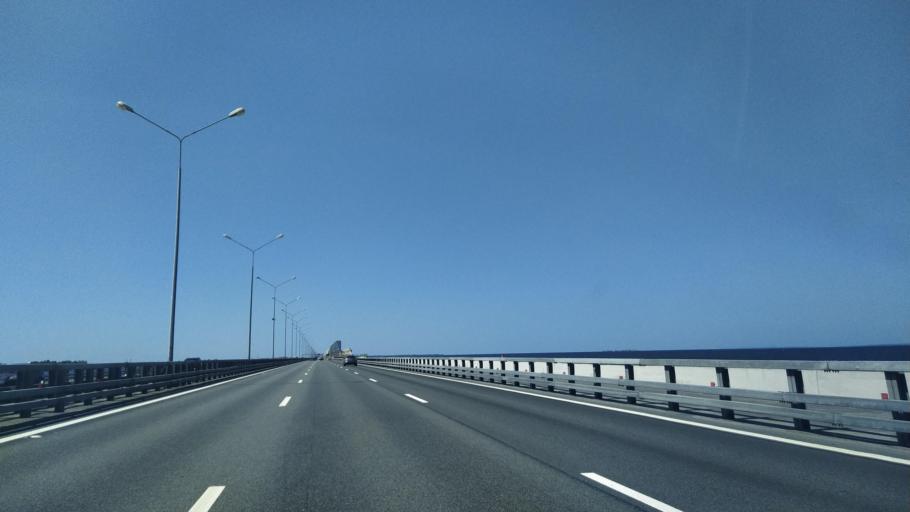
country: RU
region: Leningrad
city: Gorskaya
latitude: 60.0329
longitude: 29.9197
